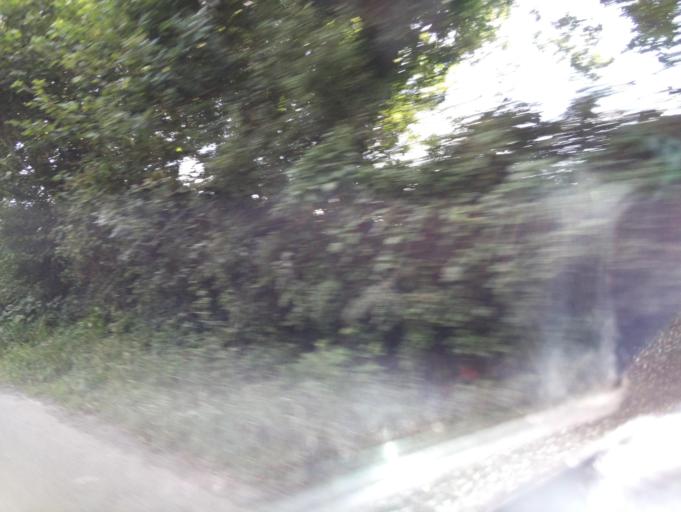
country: GB
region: England
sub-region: Cornwall
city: Saltash
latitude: 50.4268
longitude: -4.2529
